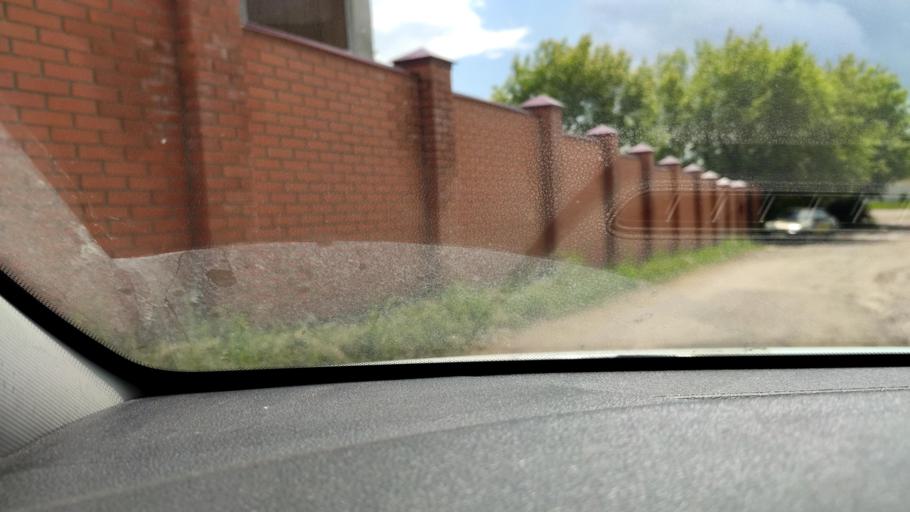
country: RU
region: Tatarstan
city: Vysokaya Gora
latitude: 55.8134
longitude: 49.2730
